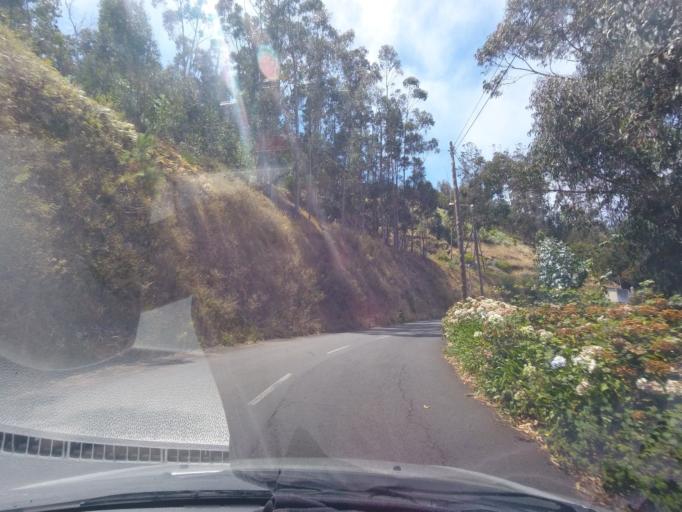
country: PT
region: Madeira
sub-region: Santa Cruz
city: Camacha
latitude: 32.6877
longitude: -16.8294
